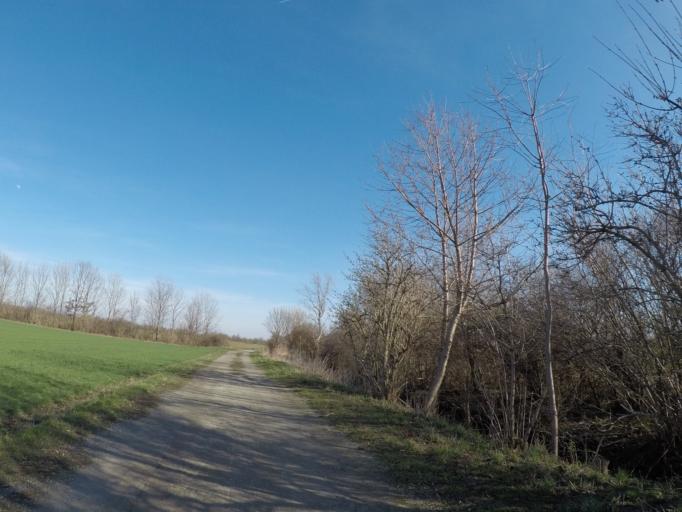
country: AT
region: Lower Austria
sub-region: Politischer Bezirk Modling
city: Biedermannsdorf
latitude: 48.1007
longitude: 16.3340
